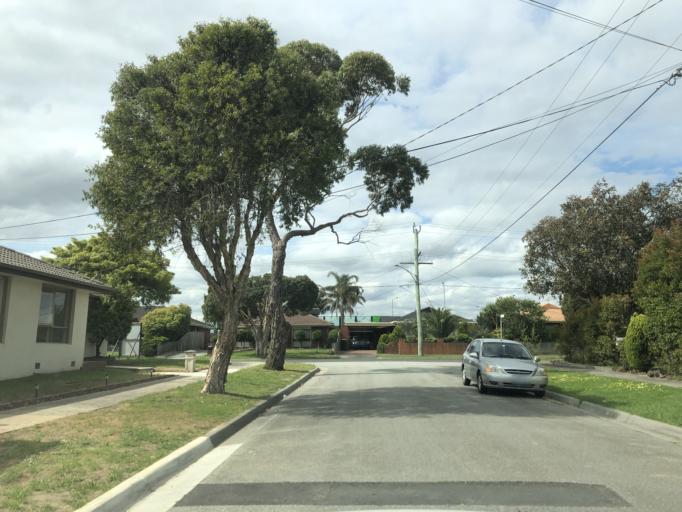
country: AU
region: Victoria
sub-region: Greater Dandenong
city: Noble Park North
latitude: -37.9440
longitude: 145.2000
